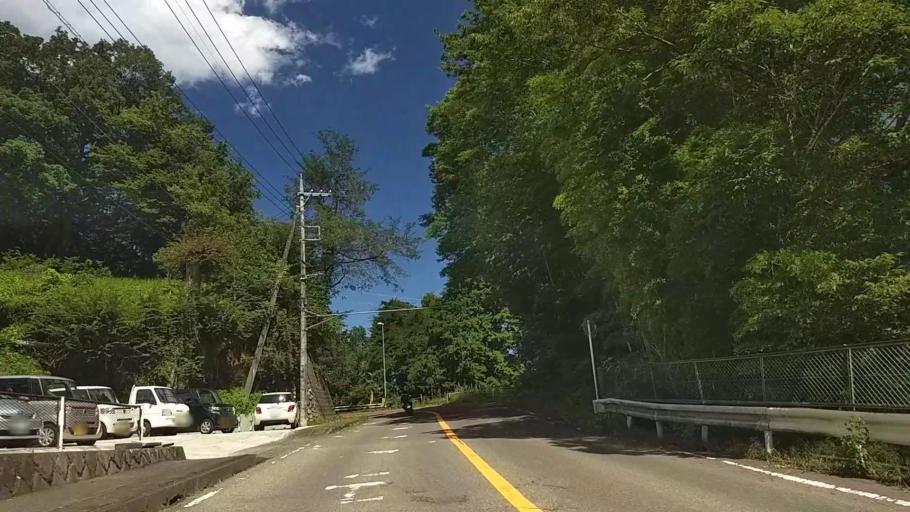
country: JP
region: Tokyo
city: Hachioji
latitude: 35.5679
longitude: 139.2742
